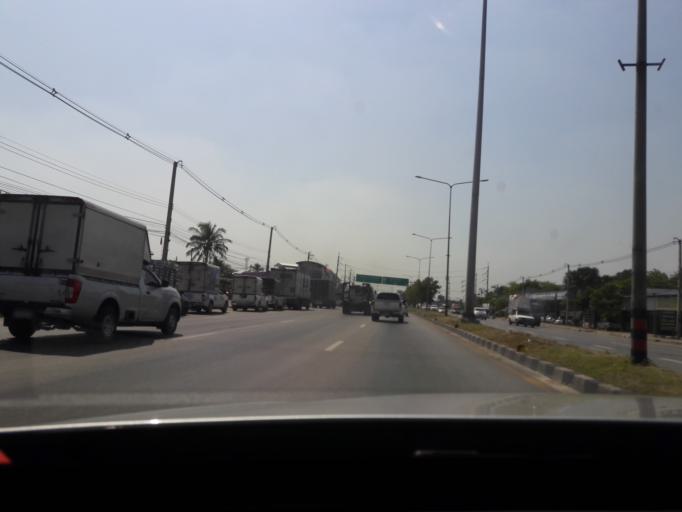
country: TH
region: Samut Sakhon
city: Krathum Baen
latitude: 13.6511
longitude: 100.3035
